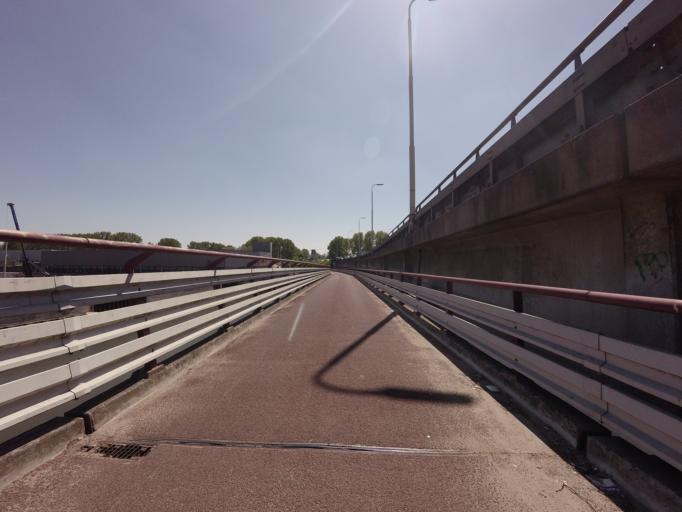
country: NL
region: South Holland
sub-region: Gemeente Papendrecht
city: Papendrecht
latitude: 51.8194
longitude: 4.7065
